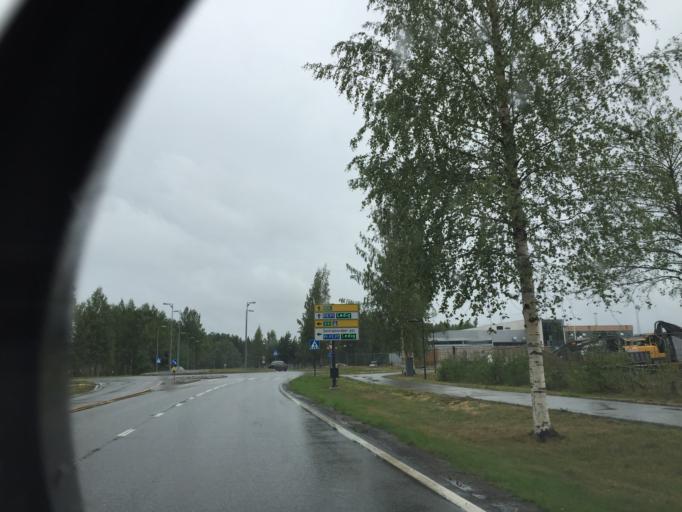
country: NO
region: Akershus
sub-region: Nannestad
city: Teigebyen
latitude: 60.1864
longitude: 11.0895
